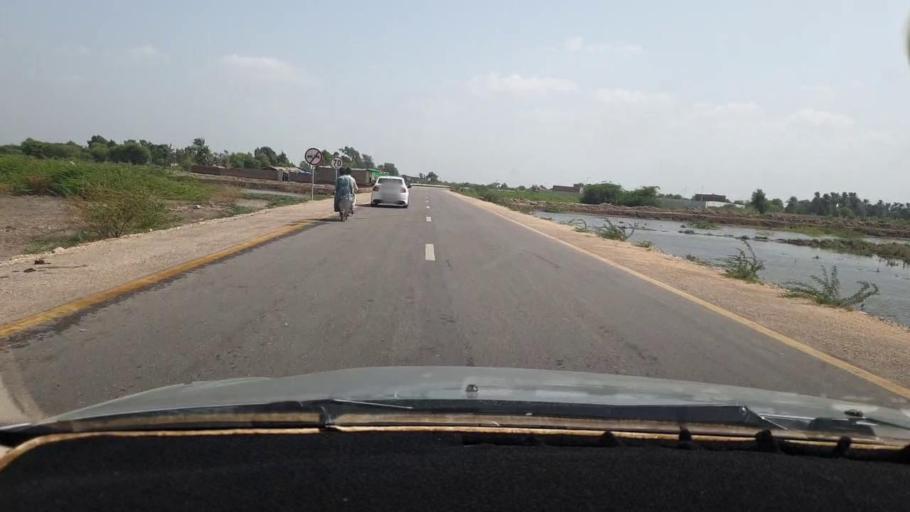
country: PK
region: Sindh
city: Digri
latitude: 25.1533
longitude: 69.1245
